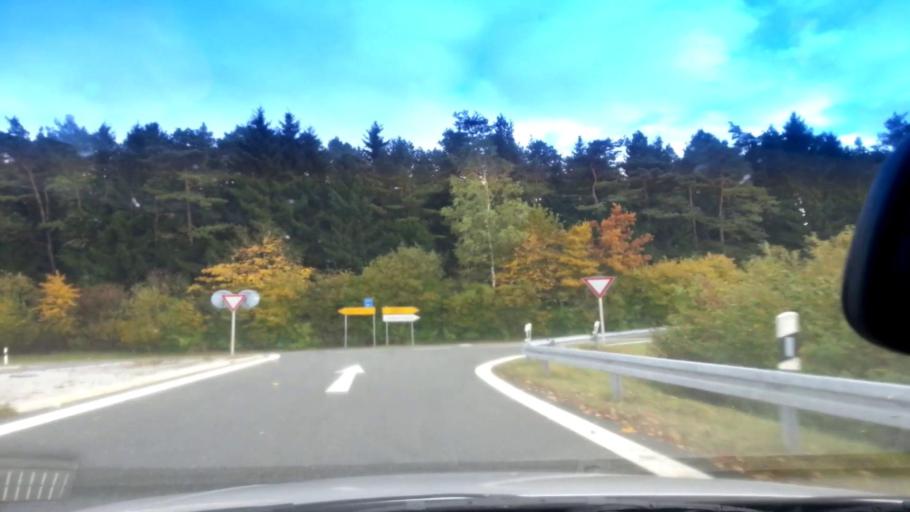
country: DE
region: Bavaria
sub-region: Upper Franconia
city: Kasendorf
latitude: 50.0110
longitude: 11.3213
